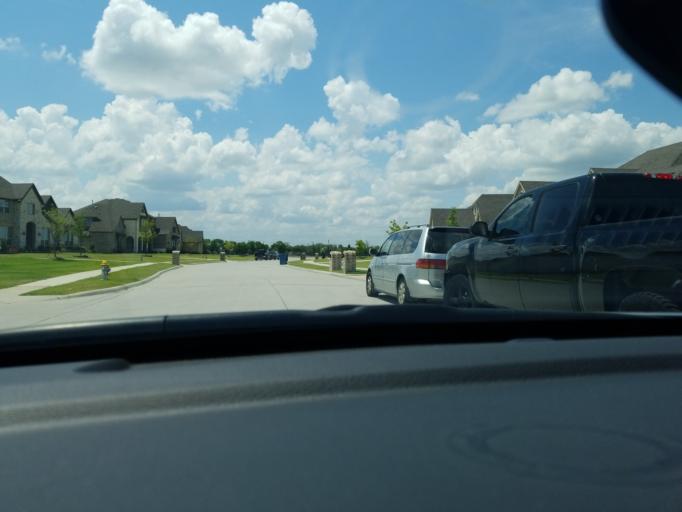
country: US
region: Texas
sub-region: Dallas County
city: Sunnyvale
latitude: 32.8131
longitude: -96.5734
